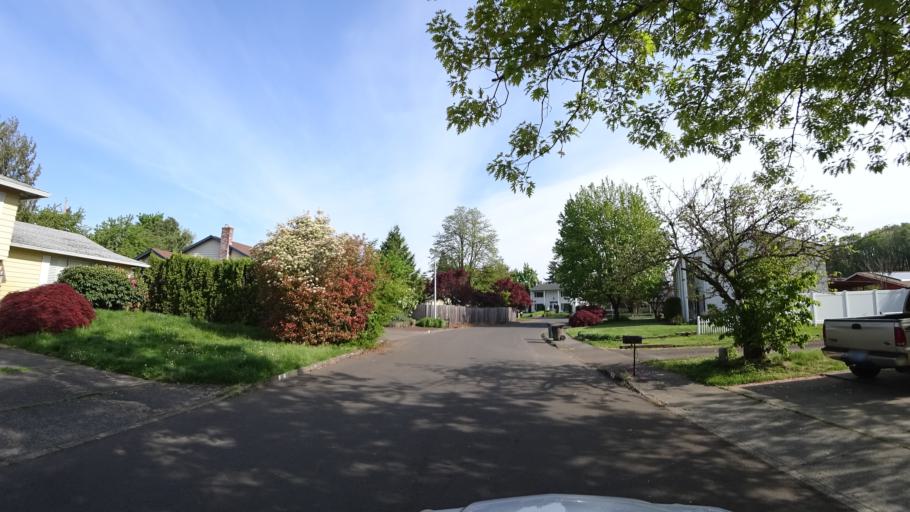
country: US
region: Oregon
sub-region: Washington County
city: Hillsboro
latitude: 45.5253
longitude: -122.9625
